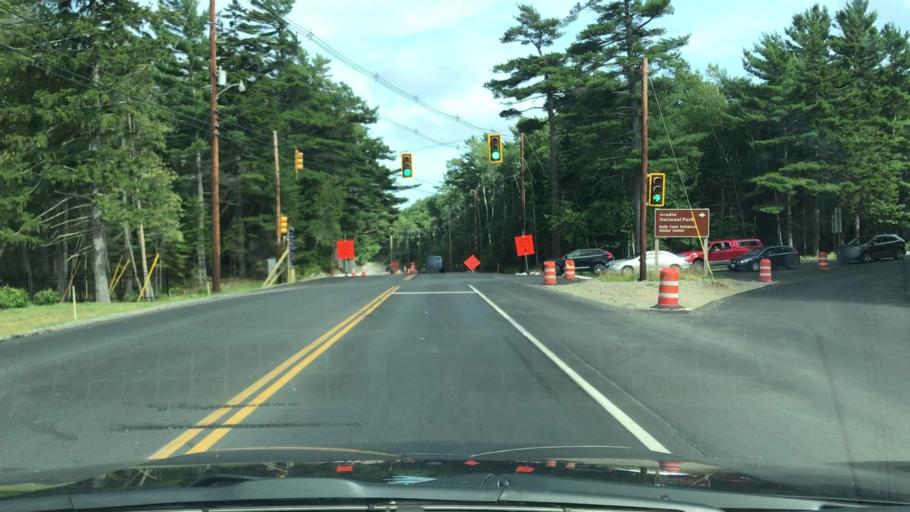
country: US
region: Maine
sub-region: Hancock County
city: Bar Harbor
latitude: 44.4105
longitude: -68.2465
